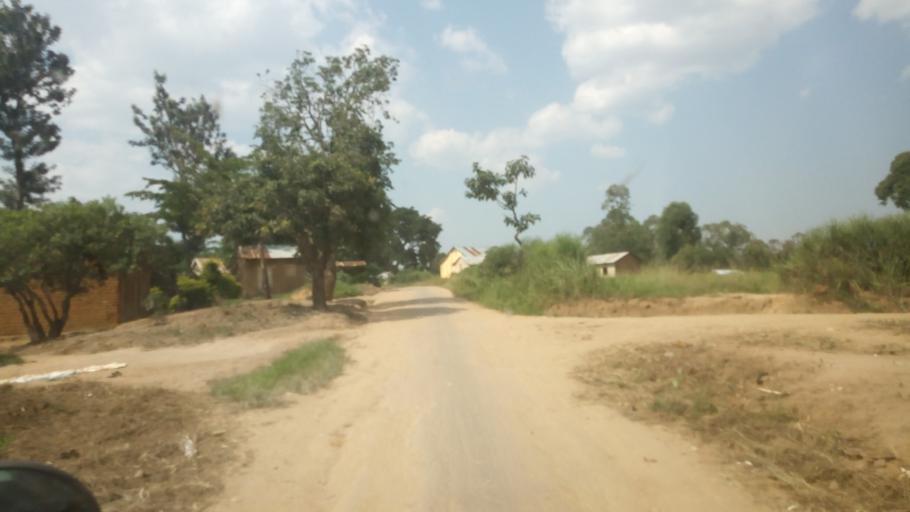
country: UG
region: Western Region
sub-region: Kanungu District
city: Ntungamo
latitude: -0.7894
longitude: 29.6868
